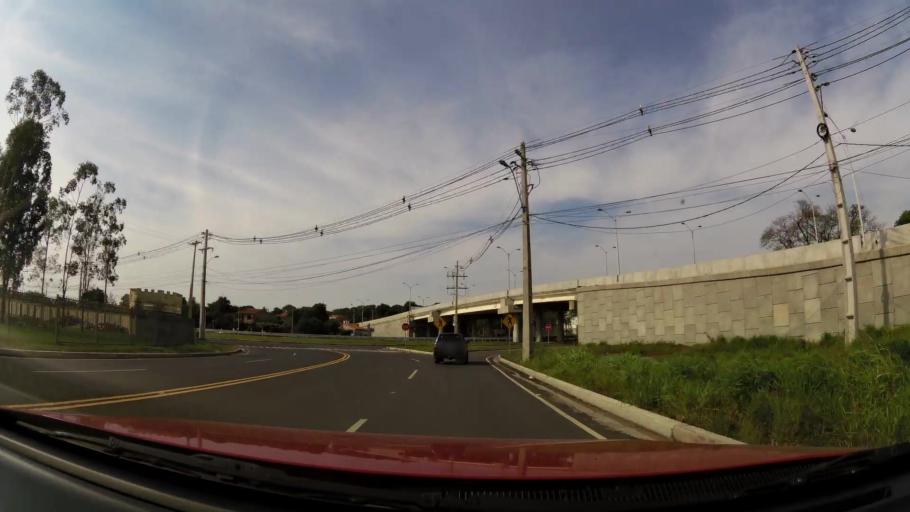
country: PY
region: Central
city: Fernando de la Mora
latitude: -25.2559
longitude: -57.5512
